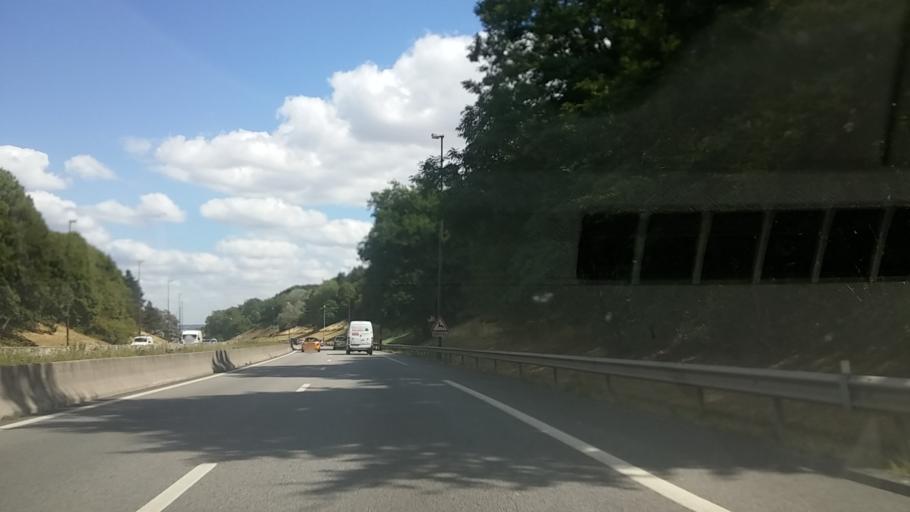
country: FR
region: Ile-de-France
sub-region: Departement des Hauts-de-Seine
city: Chatenay-Malabry
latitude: 48.7610
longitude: 2.2518
